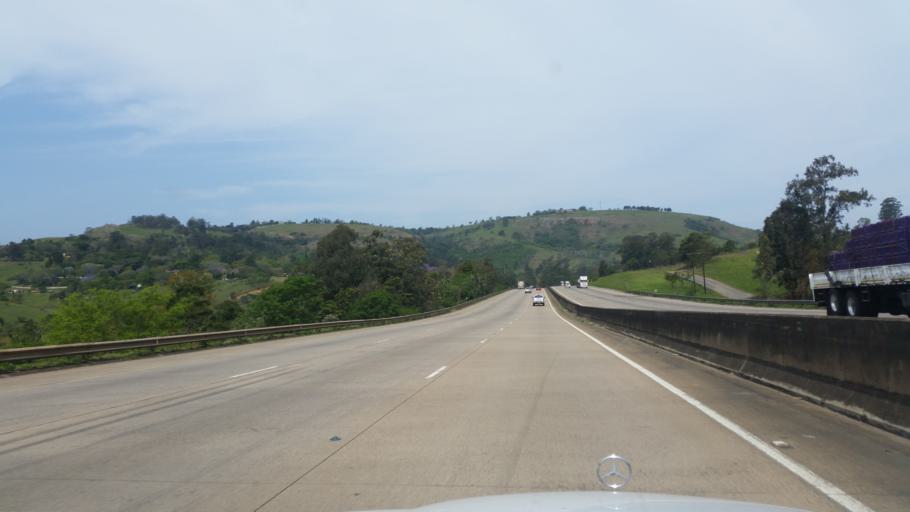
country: ZA
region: KwaZulu-Natal
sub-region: eThekwini Metropolitan Municipality
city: Mpumalanga
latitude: -29.7383
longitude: 30.6529
